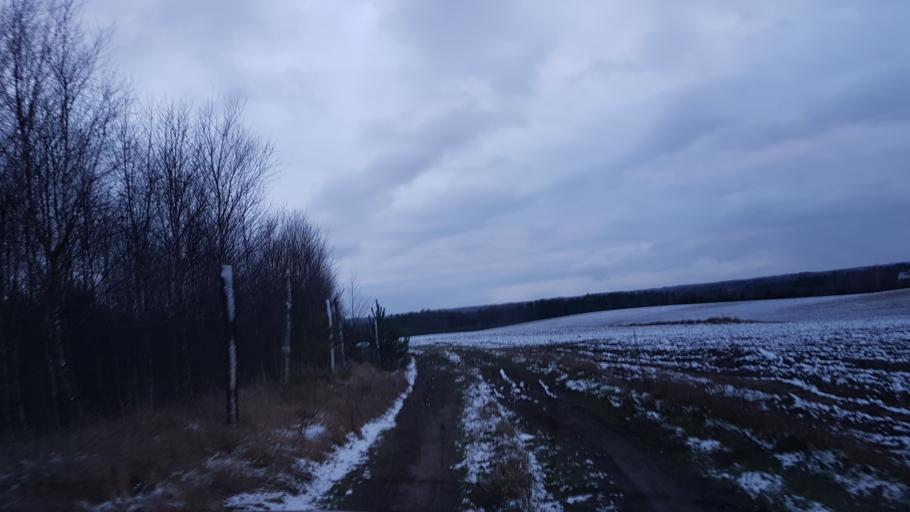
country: PL
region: Pomeranian Voivodeship
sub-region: Powiat bytowski
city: Tuchomie
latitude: 54.1505
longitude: 17.3048
